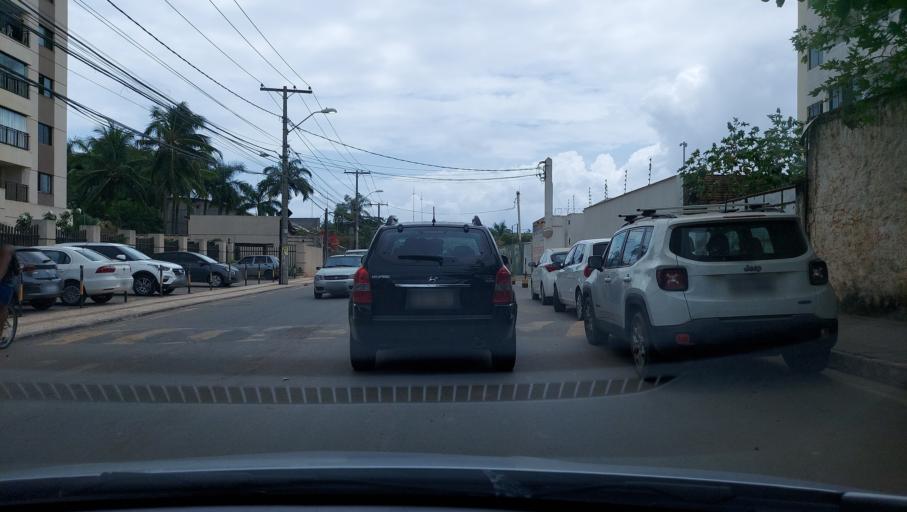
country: BR
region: Bahia
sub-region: Lauro De Freitas
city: Lauro de Freitas
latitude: -12.9374
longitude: -38.3837
